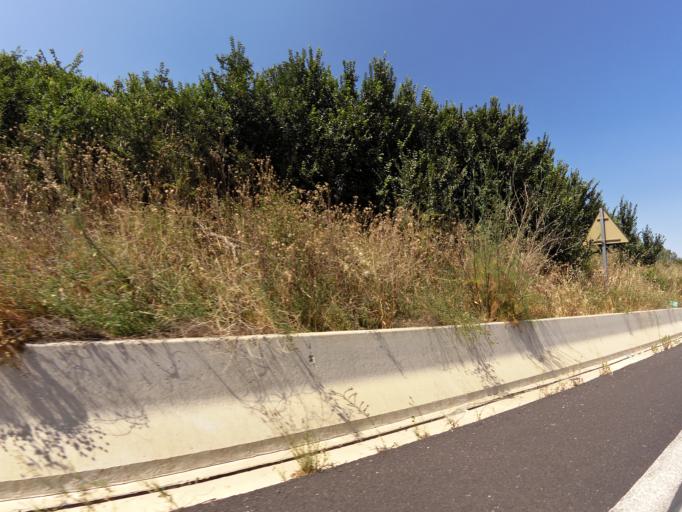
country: FR
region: Languedoc-Roussillon
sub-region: Departement de l'Herault
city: Le Cres
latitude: 43.6087
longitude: 3.9364
